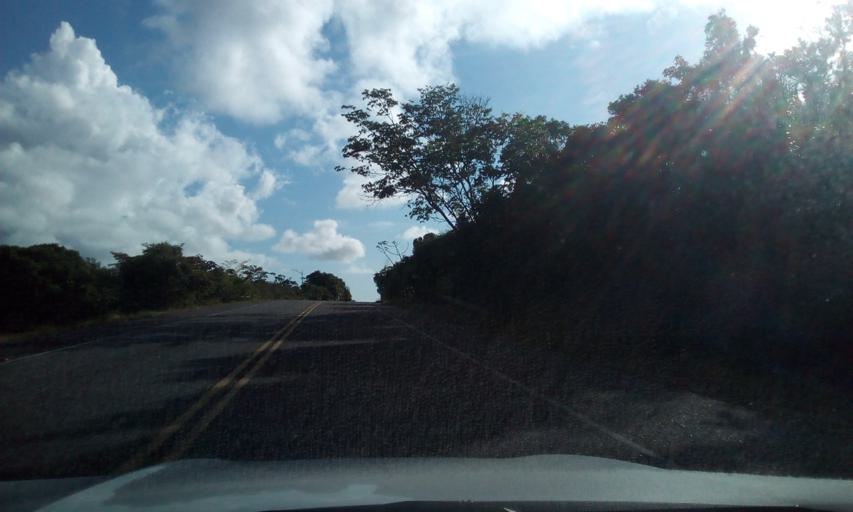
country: BR
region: Bahia
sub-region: Conde
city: Conde
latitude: -12.0838
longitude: -37.7691
